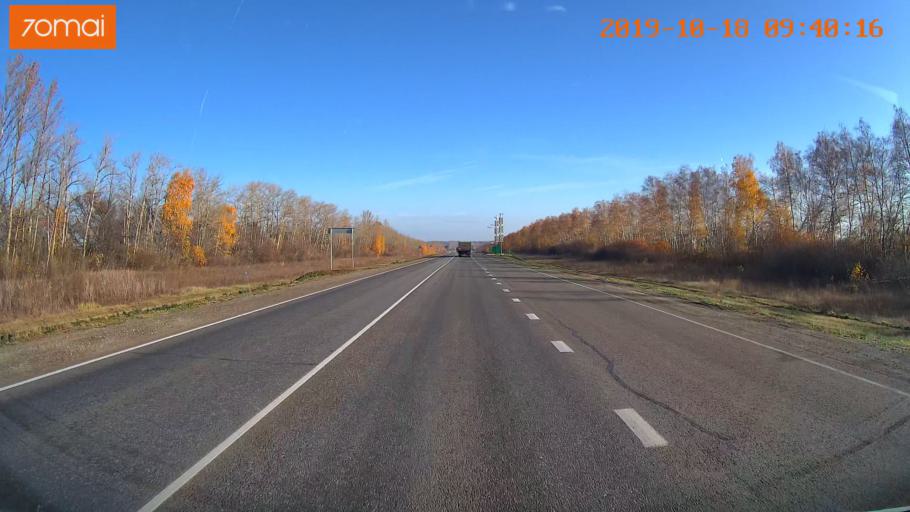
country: RU
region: Tula
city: Yefremov
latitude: 53.2621
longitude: 38.1458
